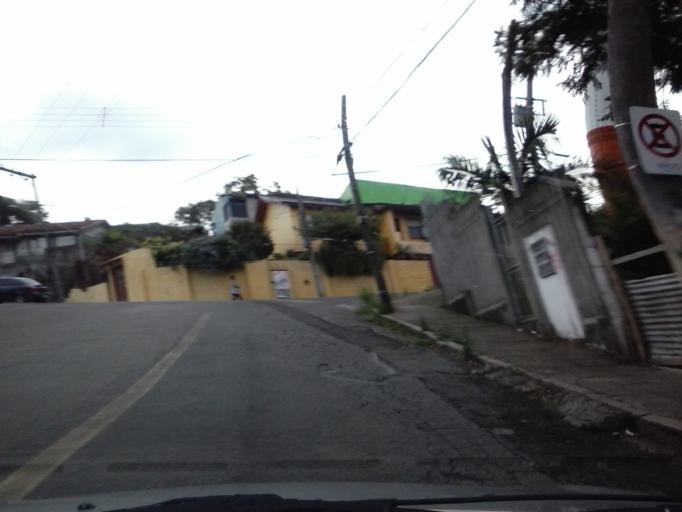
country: BR
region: Rio Grande do Sul
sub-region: Porto Alegre
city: Porto Alegre
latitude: -30.0517
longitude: -51.1510
